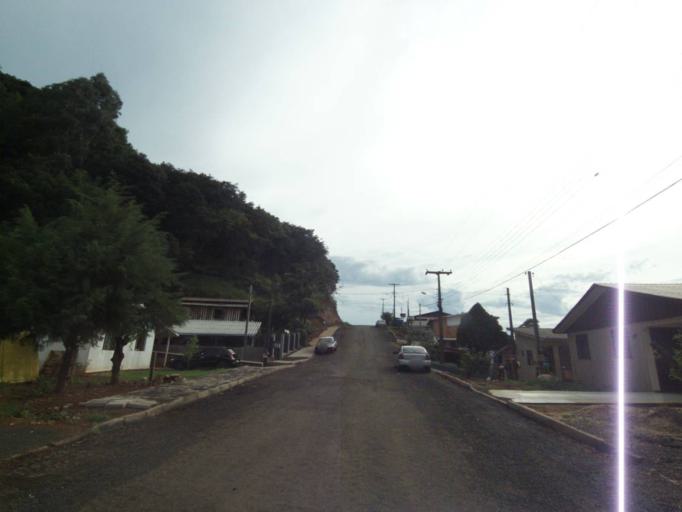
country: BR
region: Parana
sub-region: Guaraniacu
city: Guaraniacu
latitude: -25.1013
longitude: -52.8751
